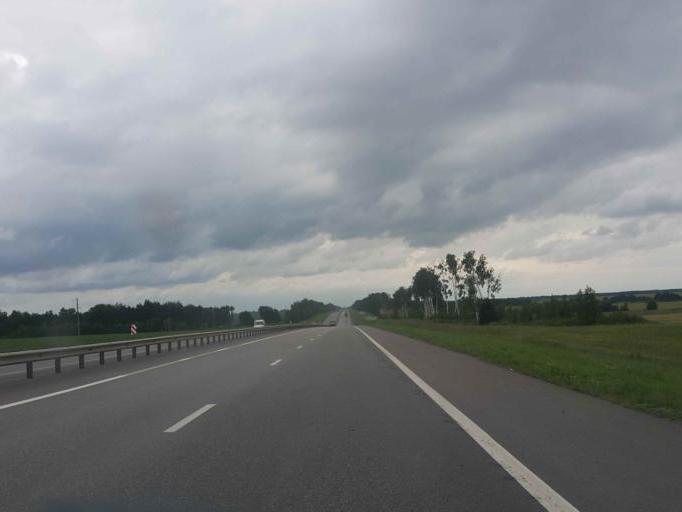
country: RU
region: Tambov
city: Selezni
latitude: 52.8160
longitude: 40.9392
